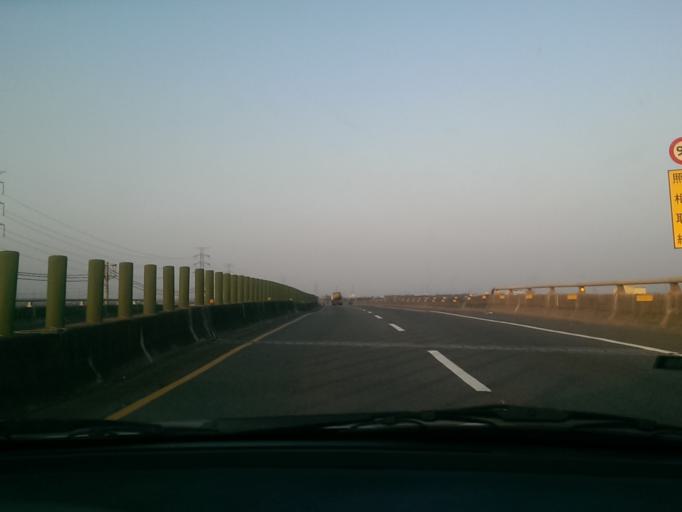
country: TW
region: Taiwan
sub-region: Changhua
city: Chang-hua
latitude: 24.1743
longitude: 120.4778
